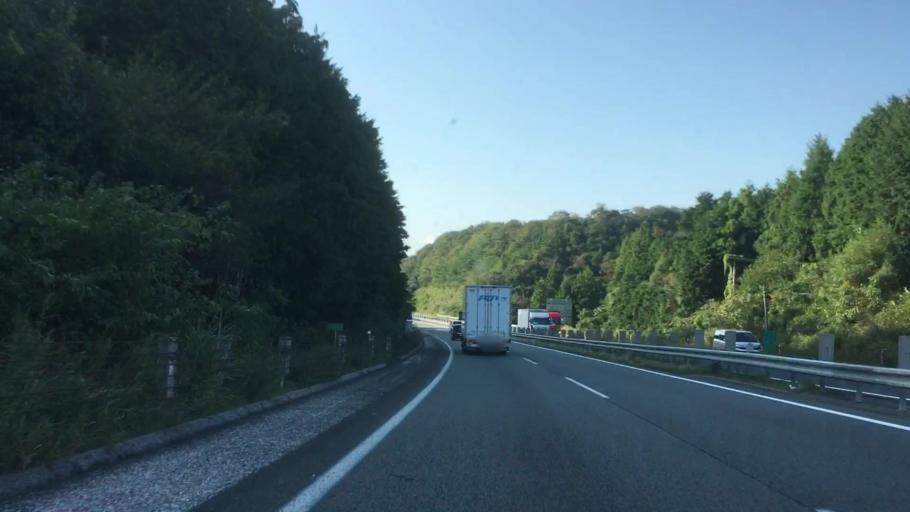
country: JP
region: Yamaguchi
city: Ogori-shimogo
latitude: 34.1594
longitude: 131.3309
